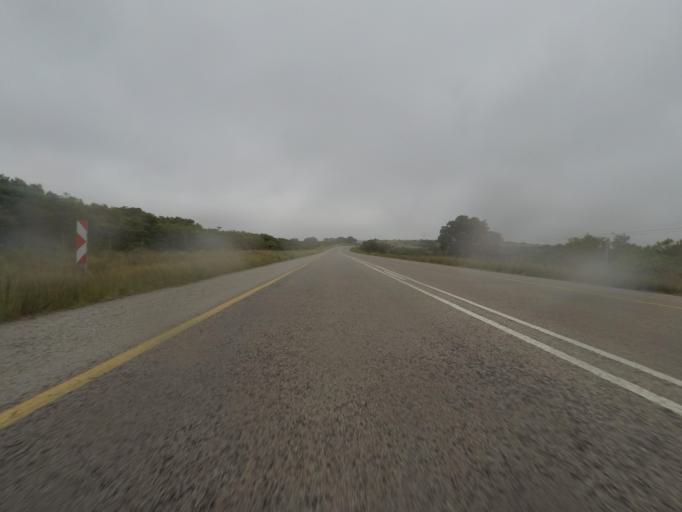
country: ZA
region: Eastern Cape
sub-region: Cacadu District Municipality
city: Grahamstown
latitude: -33.6426
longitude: 26.3655
